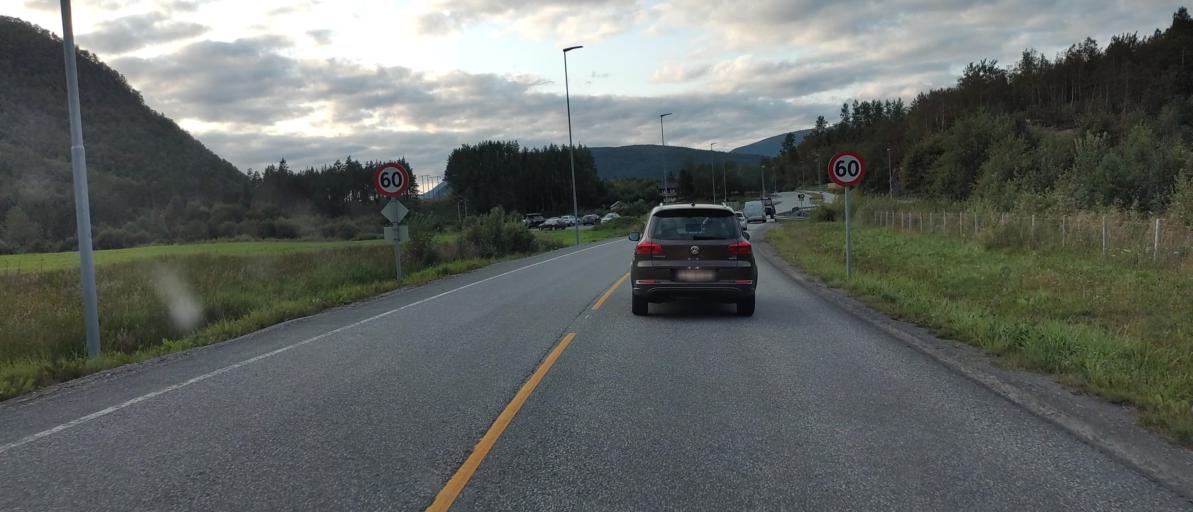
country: NO
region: More og Romsdal
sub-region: Molde
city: Molde
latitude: 62.7908
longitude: 7.2329
